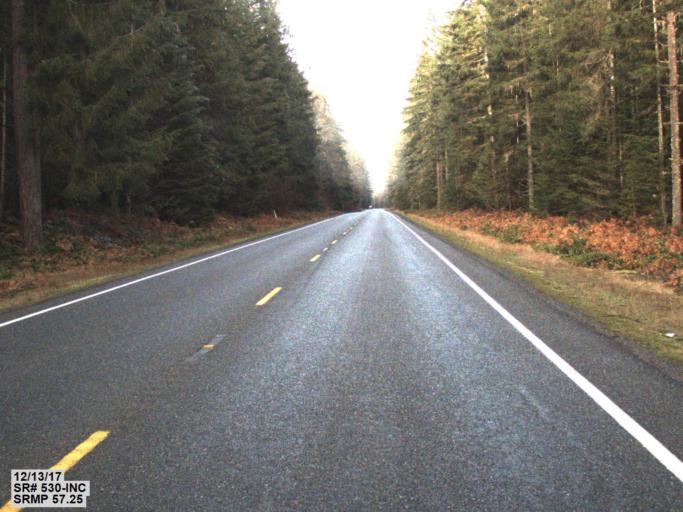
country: US
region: Washington
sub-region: Snohomish County
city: Darrington
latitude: 48.3542
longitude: -121.5399
